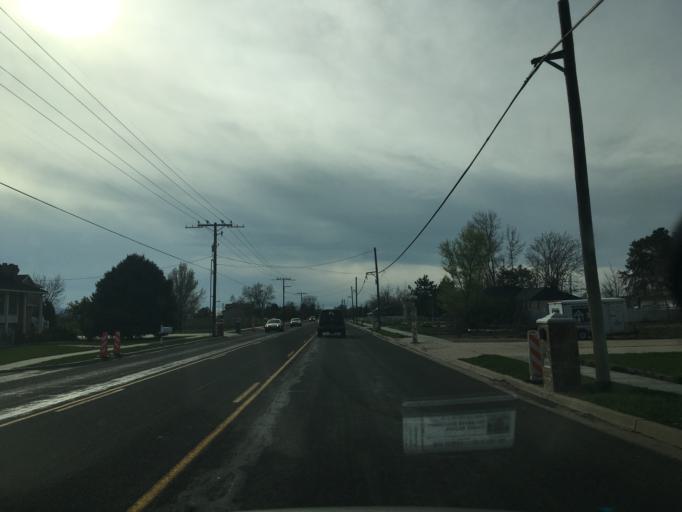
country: US
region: Utah
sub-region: Davis County
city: Layton
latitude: 41.0601
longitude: -111.9918
